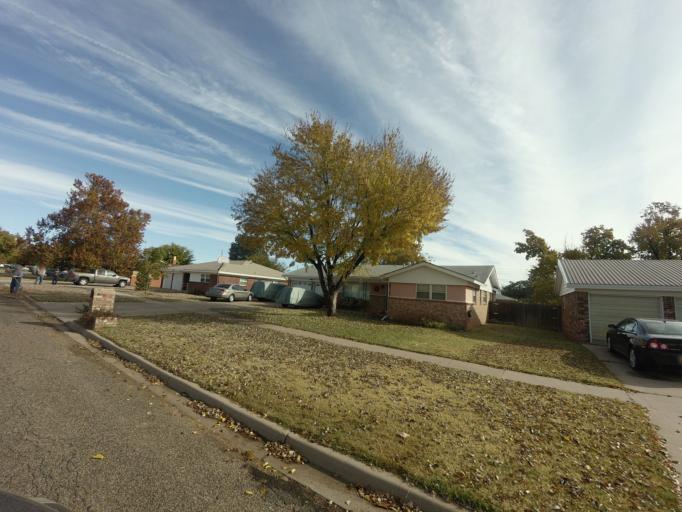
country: US
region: New Mexico
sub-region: Curry County
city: Clovis
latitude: 34.4215
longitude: -103.2255
